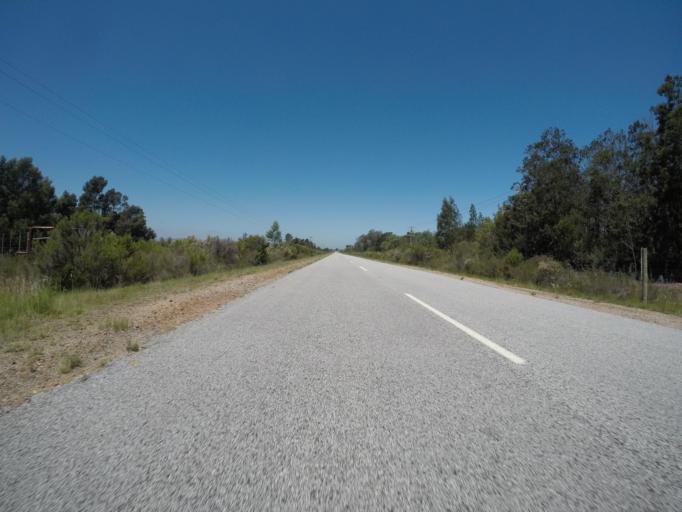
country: ZA
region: Eastern Cape
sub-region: Cacadu District Municipality
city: Kruisfontein
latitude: -33.9843
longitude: 24.5147
